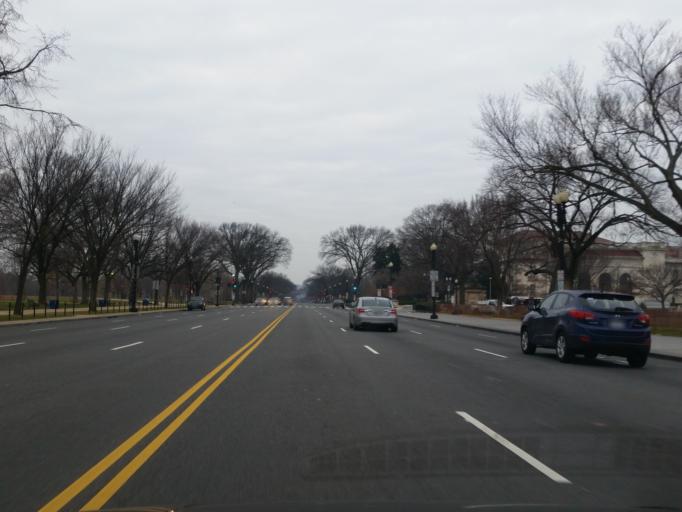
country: US
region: Washington, D.C.
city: Washington, D.C.
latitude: 38.8921
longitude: -77.0378
